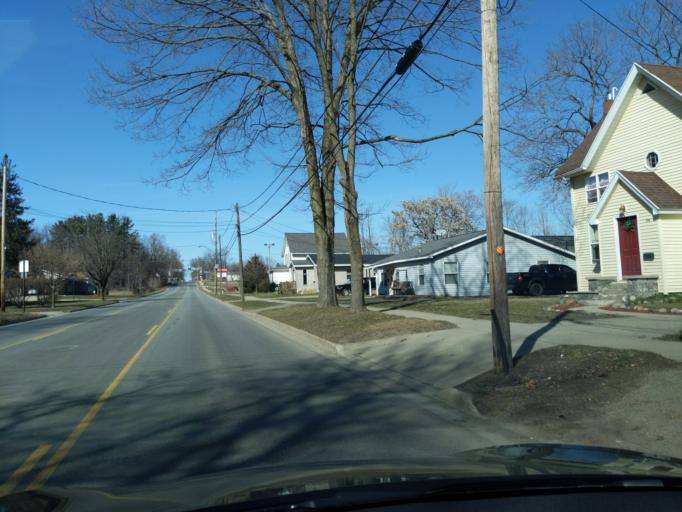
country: US
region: Michigan
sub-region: Ionia County
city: Lake Odessa
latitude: 42.7790
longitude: -85.1332
